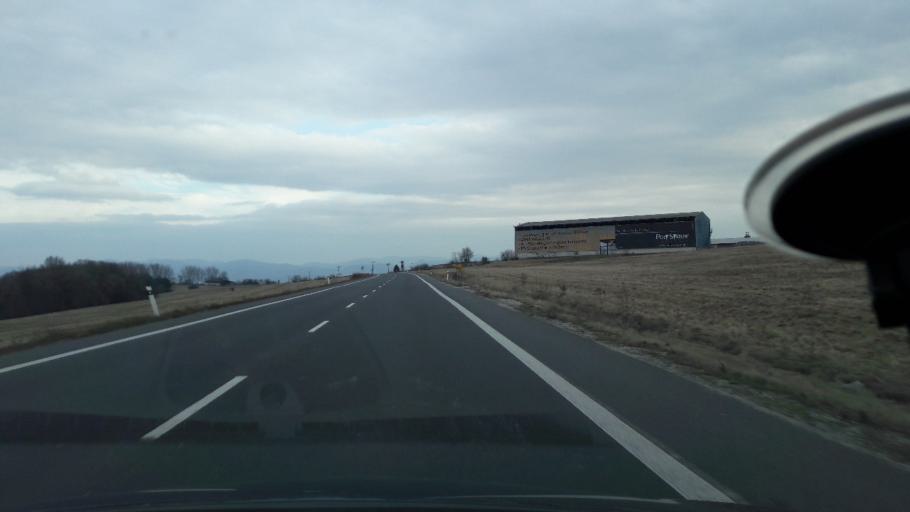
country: SK
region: Banskobystricky
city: Ziar nad Hronom
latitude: 48.6323
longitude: 18.7782
